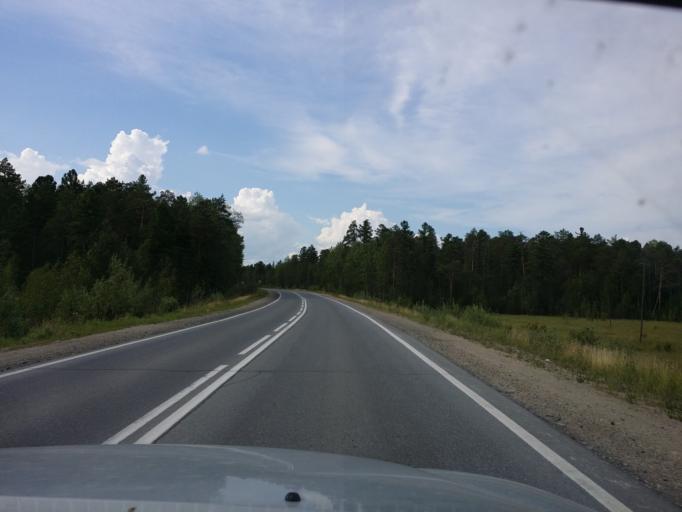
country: RU
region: Khanty-Mansiyskiy Avtonomnyy Okrug
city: Megion
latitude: 61.1223
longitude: 75.8330
